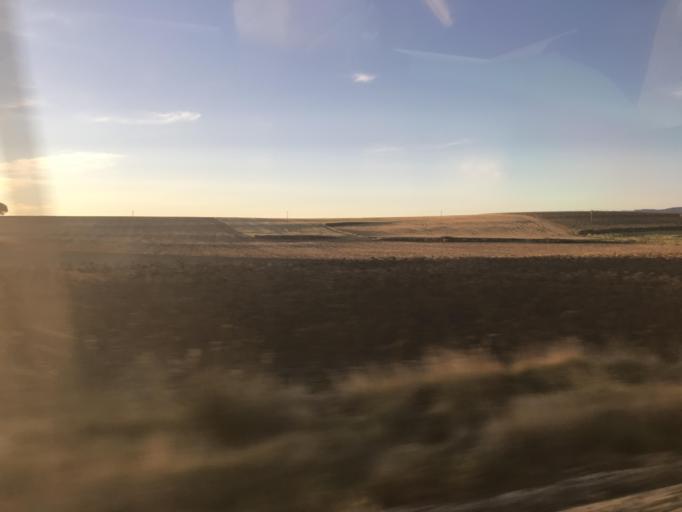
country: ES
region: Castille and Leon
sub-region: Provincia de Burgos
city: Grisalena
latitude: 42.5982
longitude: -3.2901
